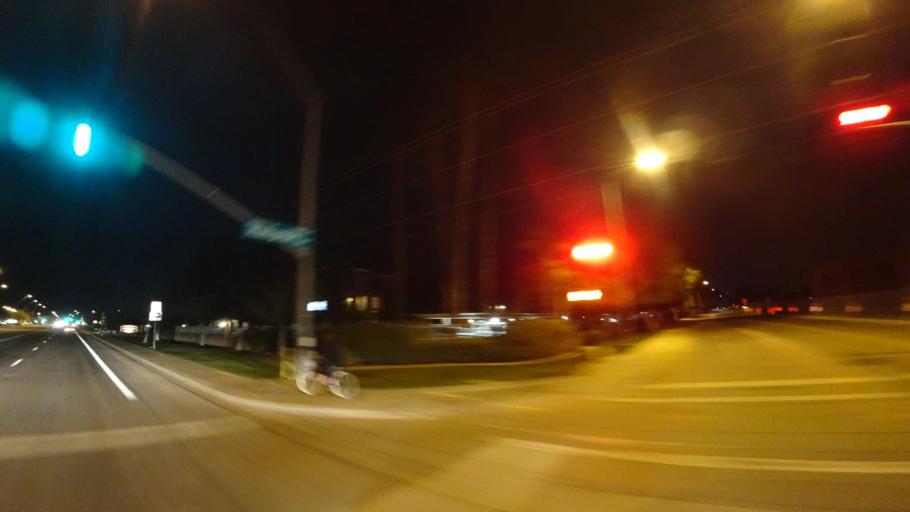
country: US
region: Arizona
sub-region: Maricopa County
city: Gilbert
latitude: 33.3901
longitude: -111.7538
